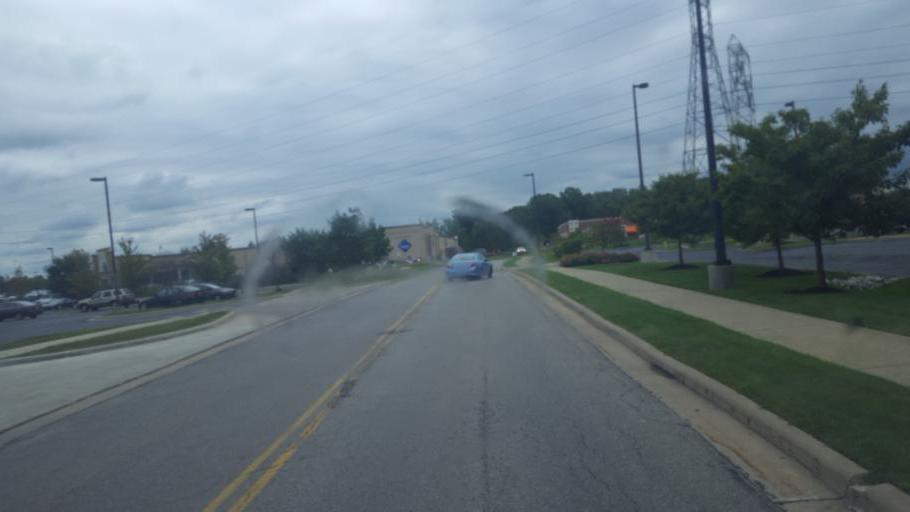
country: US
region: Ohio
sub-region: Lake County
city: Fairport Harbor
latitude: 41.7166
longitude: -81.2961
